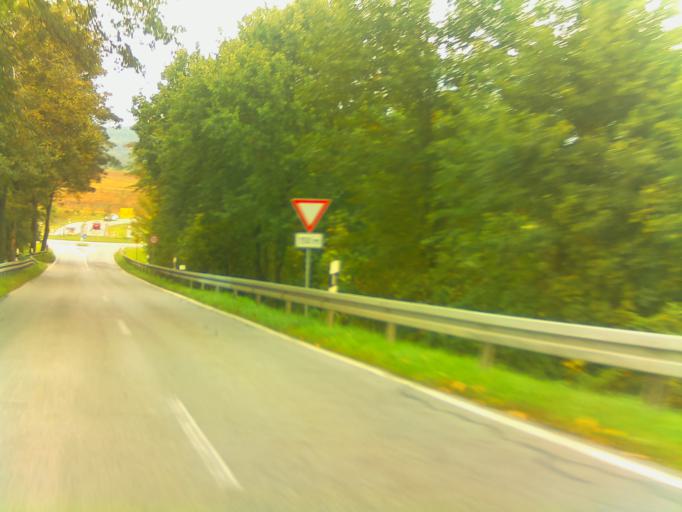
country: DE
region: Hesse
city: Hochst im Odenwald
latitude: 49.7909
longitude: 8.9857
